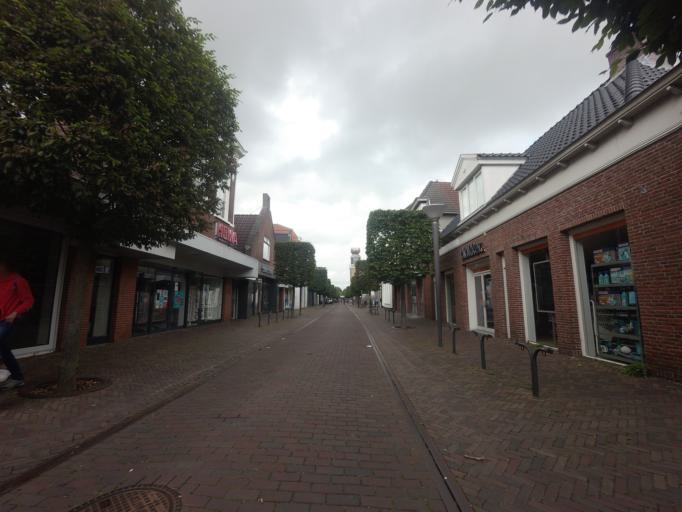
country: NL
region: Friesland
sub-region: Gemeente Skarsterlan
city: Joure
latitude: 52.9669
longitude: 5.7967
